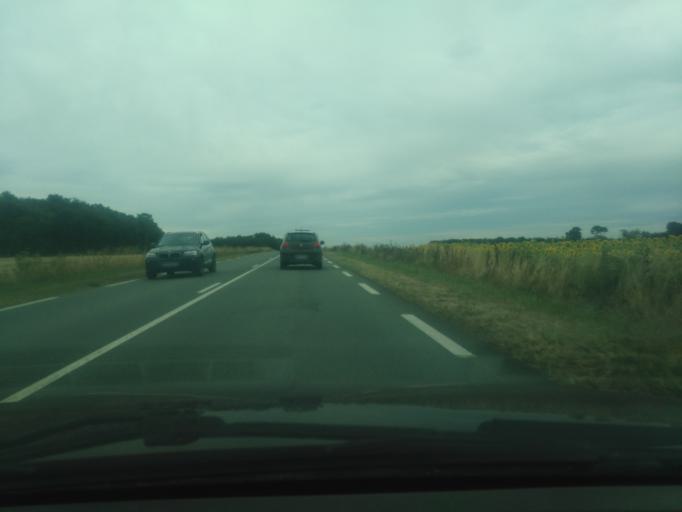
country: FR
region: Poitou-Charentes
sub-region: Departement de la Vienne
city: Saint-Savin
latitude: 46.5722
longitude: 0.8141
